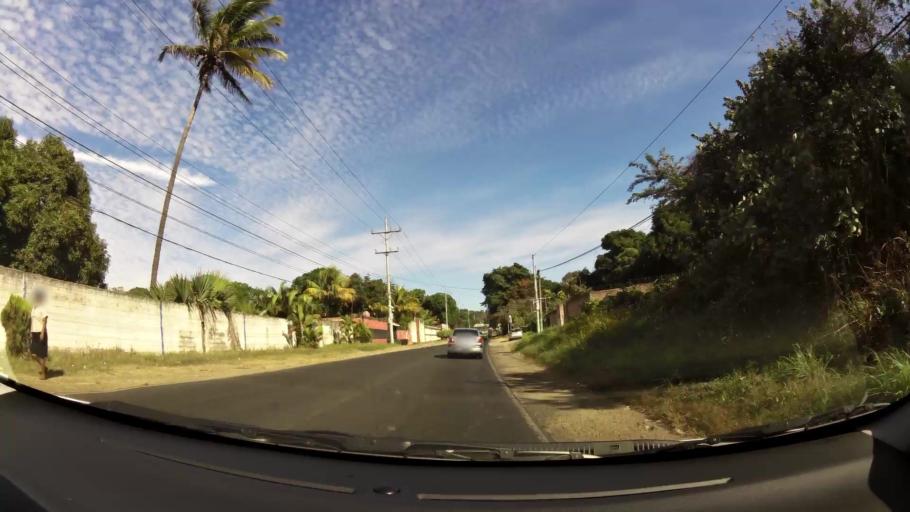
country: SV
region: Santa Ana
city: Santa Ana
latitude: 13.9853
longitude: -89.5935
